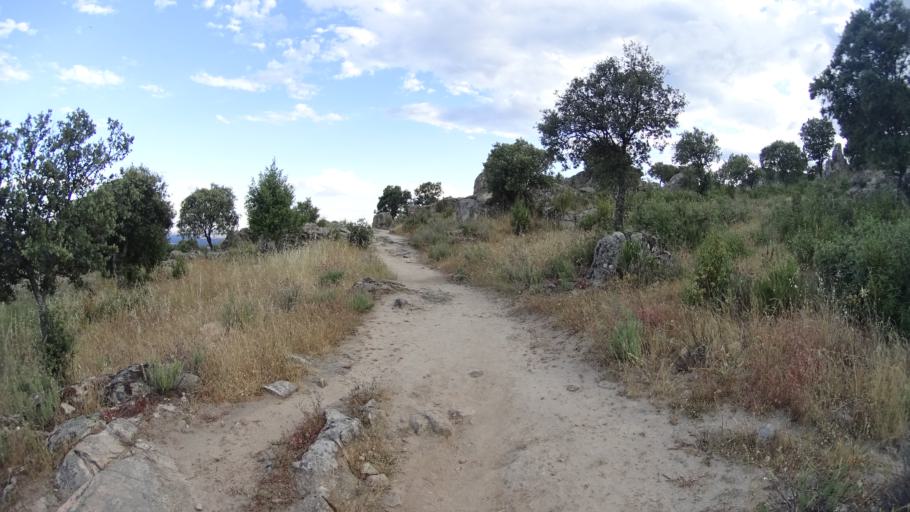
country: ES
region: Madrid
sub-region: Provincia de Madrid
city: Hoyo de Manzanares
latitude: 40.6300
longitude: -3.9118
